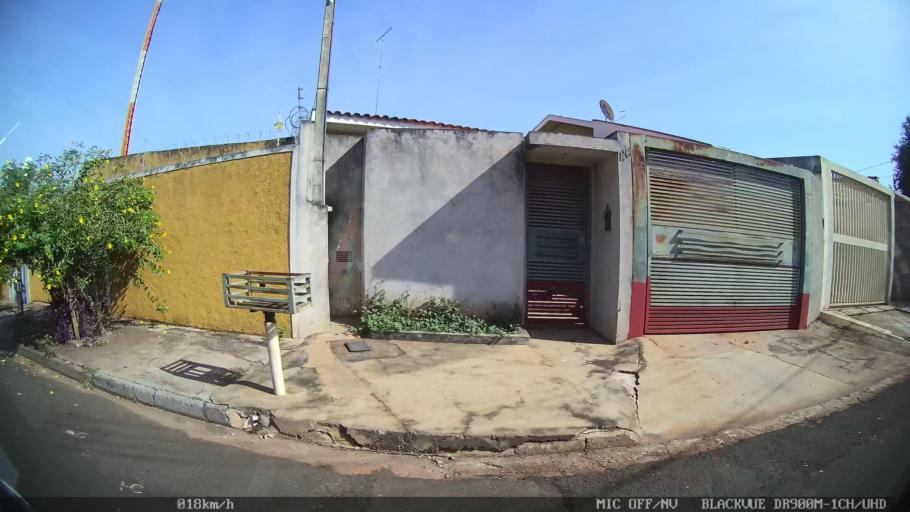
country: BR
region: Sao Paulo
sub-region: Sao Jose Do Rio Preto
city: Sao Jose do Rio Preto
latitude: -20.7905
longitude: -49.4071
